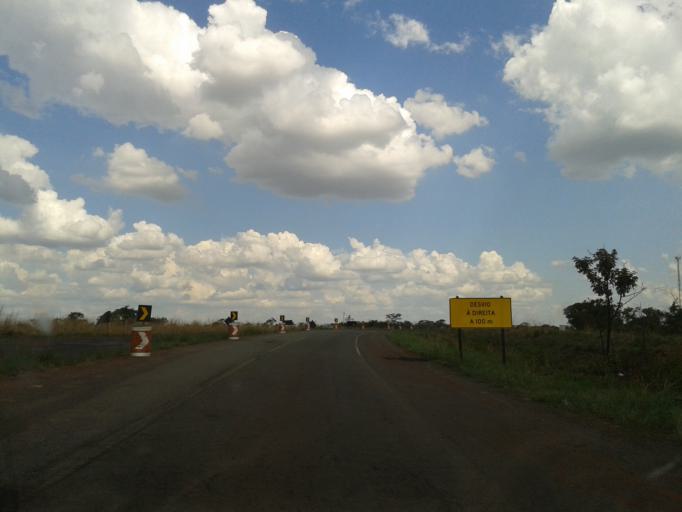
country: BR
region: Goias
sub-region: Caldas Novas
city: Caldas Novas
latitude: -17.6974
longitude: -48.7111
